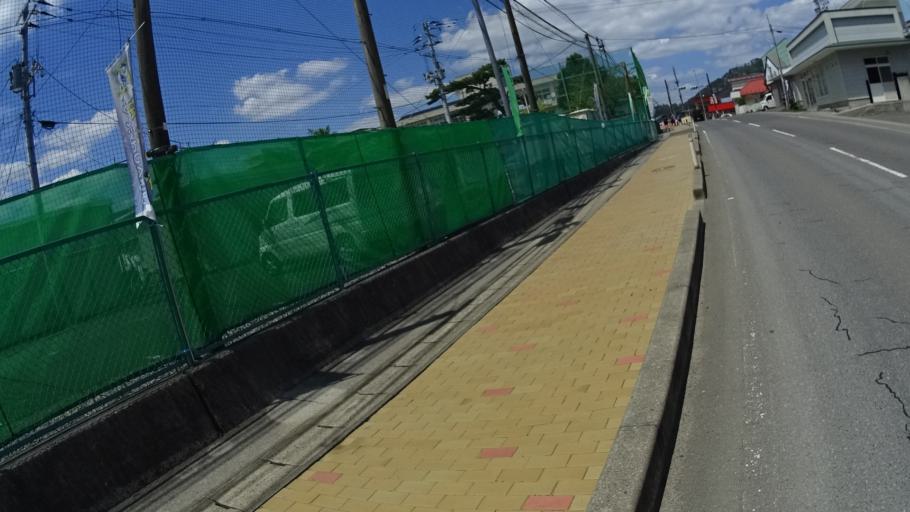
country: JP
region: Iwate
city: Ofunato
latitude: 38.8557
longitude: 141.6166
